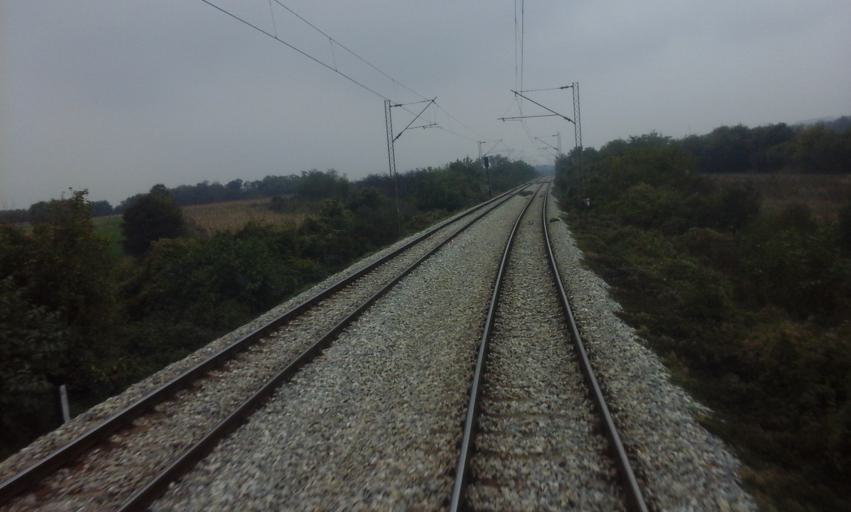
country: RS
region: Central Serbia
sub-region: Sumadijski Okrug
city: Lapovo
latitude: 44.2176
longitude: 21.0947
